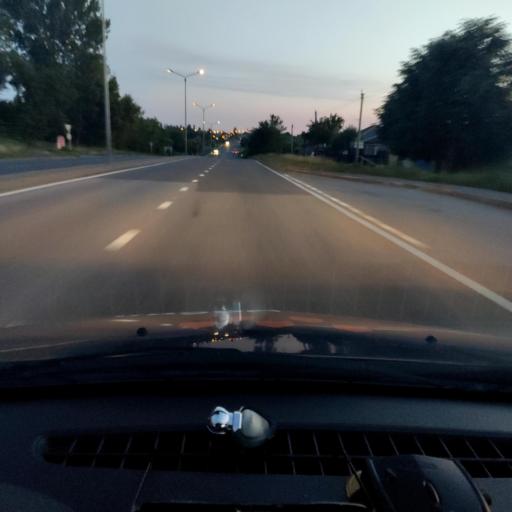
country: RU
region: Belgorod
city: Gubkin
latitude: 51.2763
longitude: 37.5910
